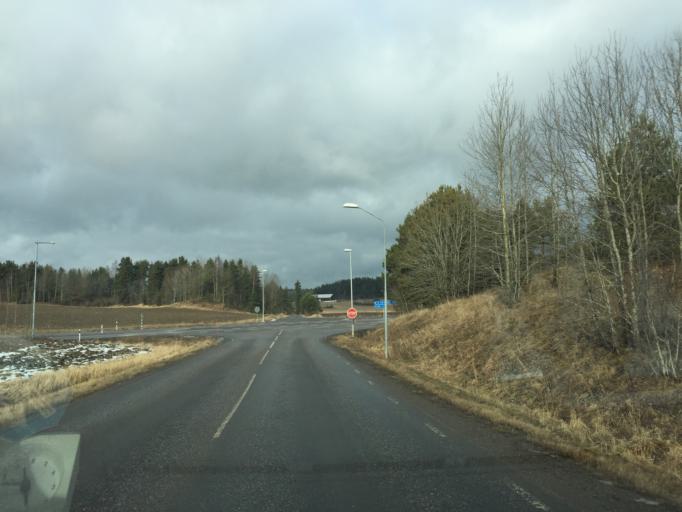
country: SE
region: Soedermanland
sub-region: Flens Kommun
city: Flen
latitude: 59.0360
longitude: 16.4537
